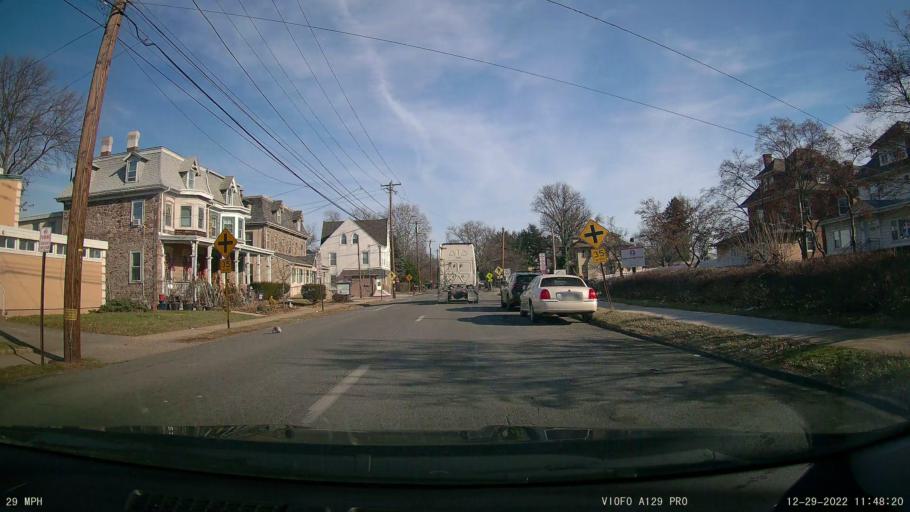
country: US
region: Pennsylvania
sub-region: Montgomery County
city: Norristown
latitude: 40.1250
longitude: -75.3310
